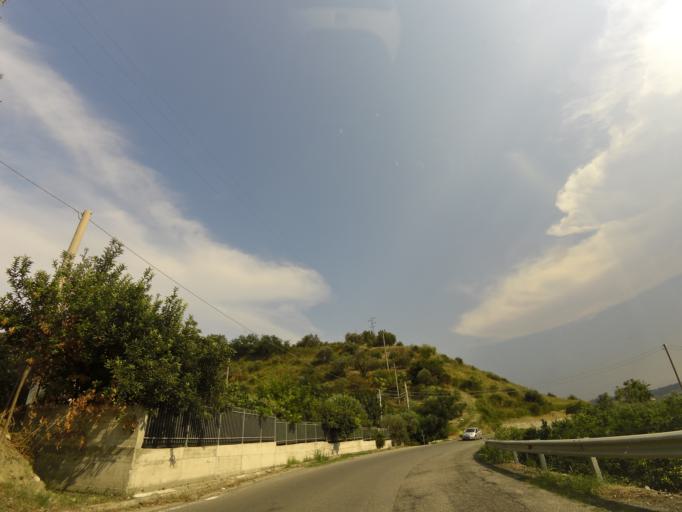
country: IT
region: Calabria
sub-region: Provincia di Reggio Calabria
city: Monasterace
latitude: 38.4553
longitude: 16.5271
